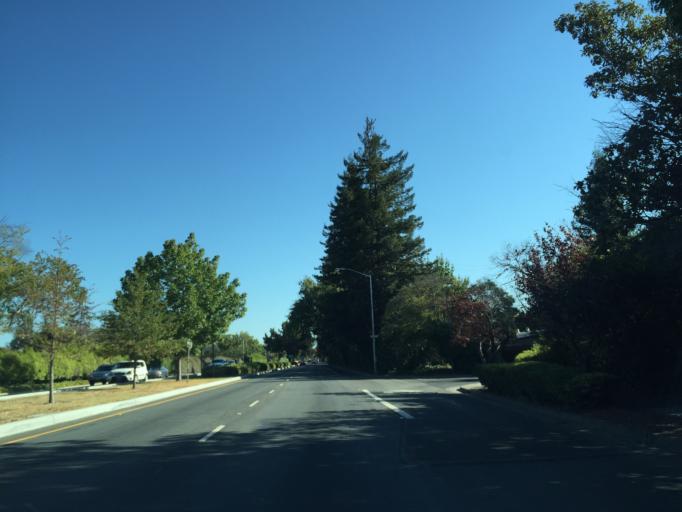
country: US
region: California
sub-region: Santa Clara County
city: Palo Alto
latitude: 37.4409
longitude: -122.1277
